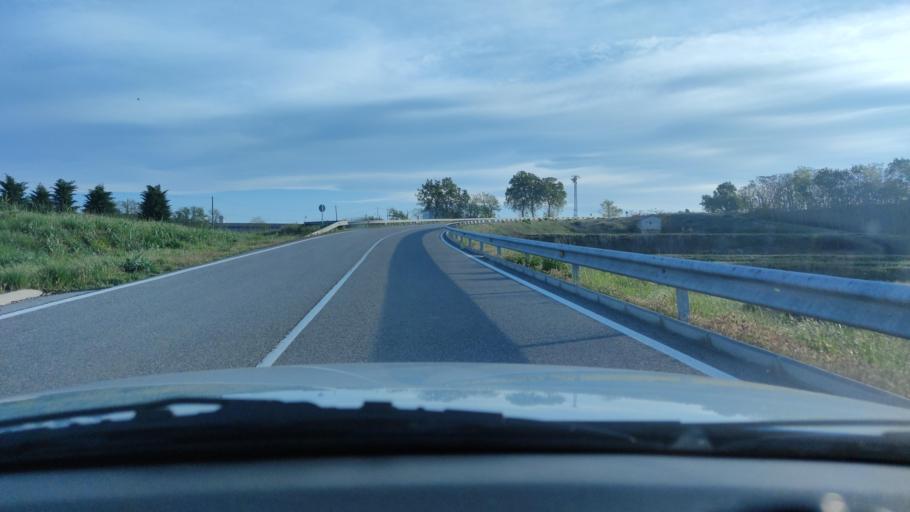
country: ES
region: Catalonia
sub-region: Provincia de Lleida
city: Castellsera
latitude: 41.7659
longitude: 1.0021
